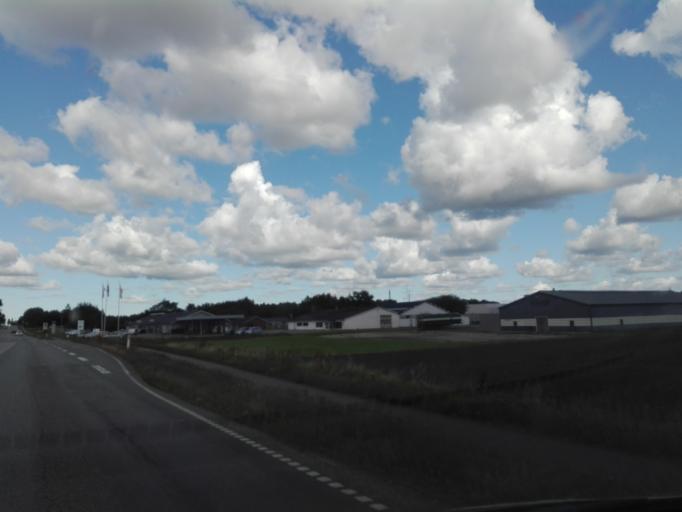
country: DK
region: North Denmark
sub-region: Mariagerfjord Kommune
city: Hobro
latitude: 56.6151
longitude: 9.8067
